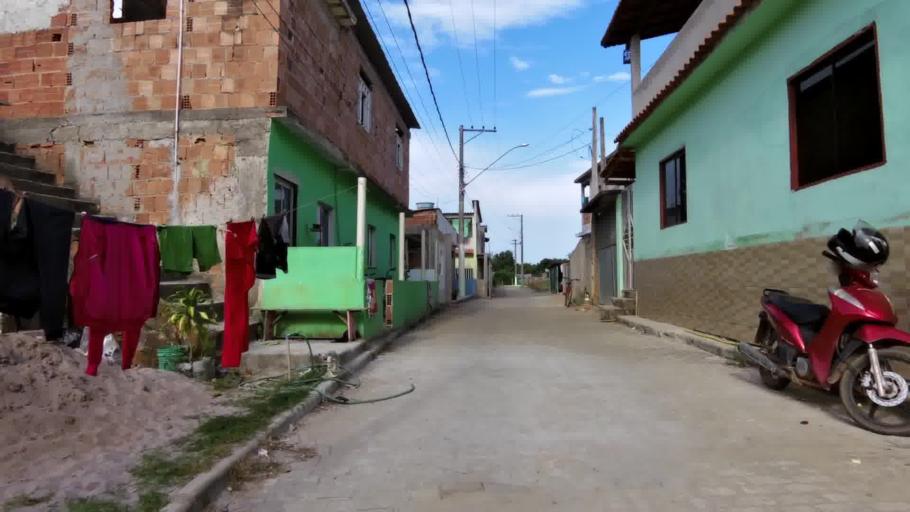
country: BR
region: Espirito Santo
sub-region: Piuma
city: Piuma
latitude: -20.8363
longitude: -40.7353
